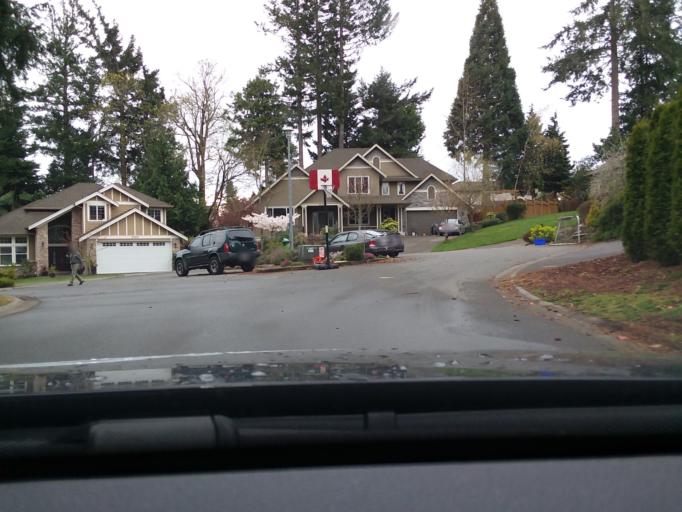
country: CA
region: British Columbia
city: Victoria
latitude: 48.5208
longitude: -123.3801
